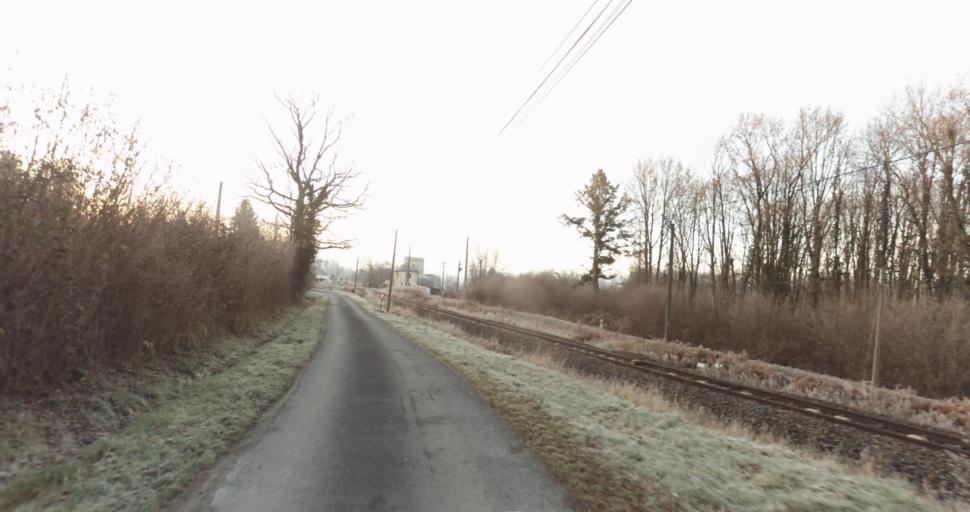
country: FR
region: Limousin
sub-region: Departement de la Haute-Vienne
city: Aixe-sur-Vienne
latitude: 45.8065
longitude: 1.1223
